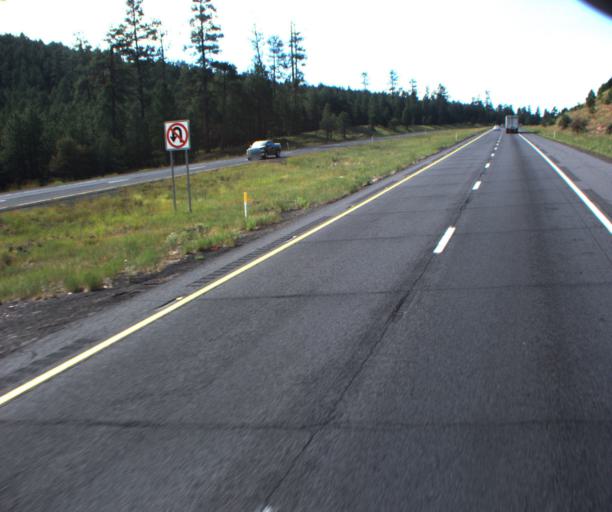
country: US
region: Arizona
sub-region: Coconino County
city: Mountainaire
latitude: 35.0386
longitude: -111.6851
